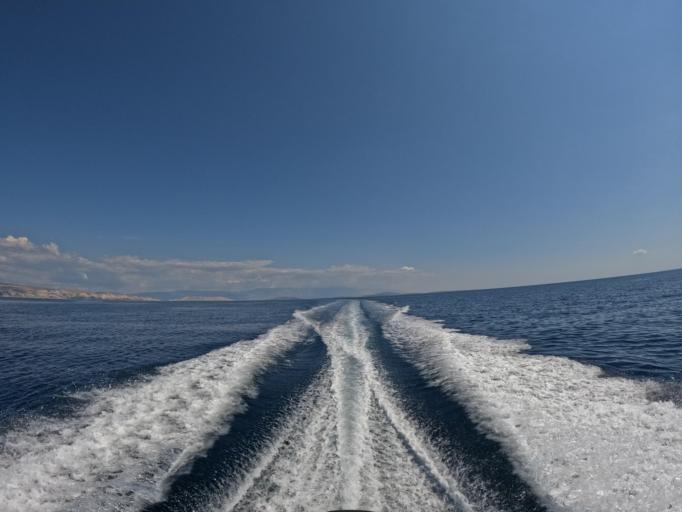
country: HR
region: Primorsko-Goranska
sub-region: Grad Krk
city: Krk
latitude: 44.9316
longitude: 14.5207
